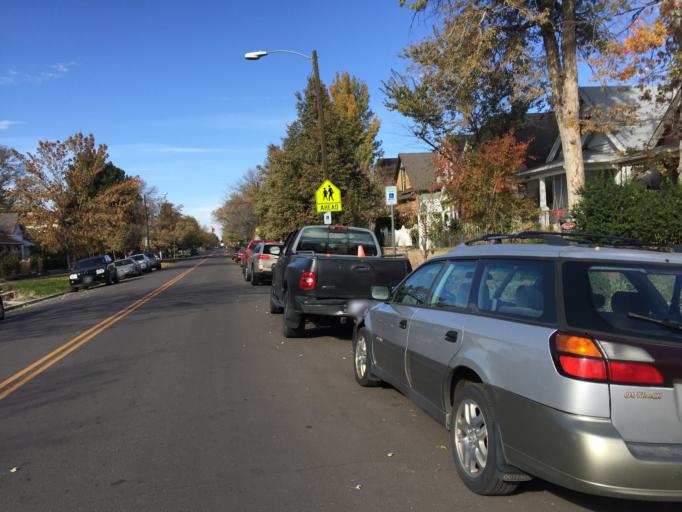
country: US
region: Colorado
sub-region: Denver County
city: Denver
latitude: 39.7609
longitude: -104.9684
